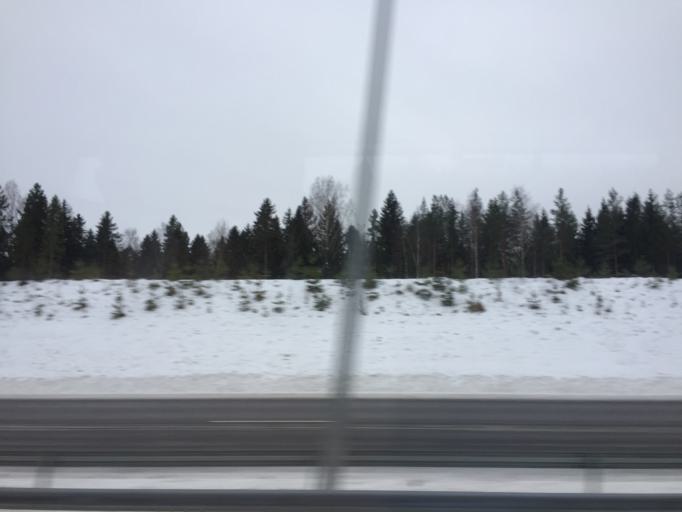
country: FI
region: Uusimaa
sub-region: Loviisa
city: Ruotsinpyhtaeae
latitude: 60.4881
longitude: 26.4707
